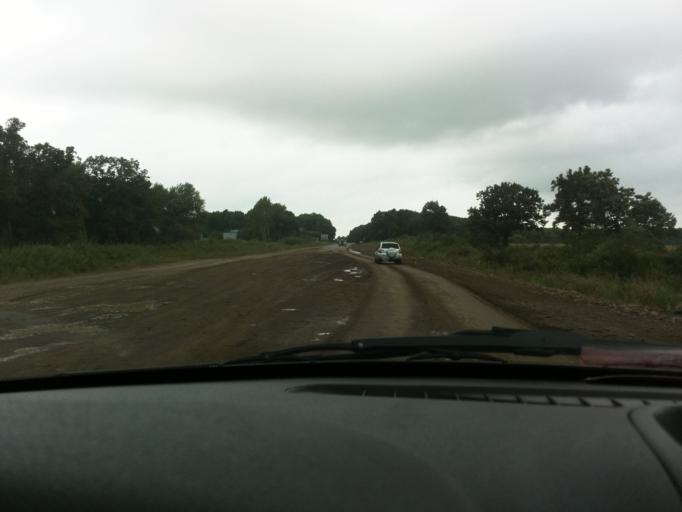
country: RU
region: Primorskiy
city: Dal'nerechensk
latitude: 45.8867
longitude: 133.7317
